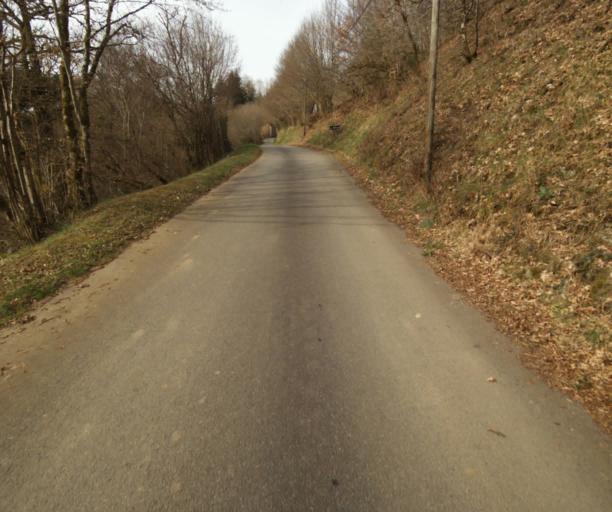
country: FR
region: Limousin
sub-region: Departement de la Correze
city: Correze
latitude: 45.4165
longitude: 1.7980
